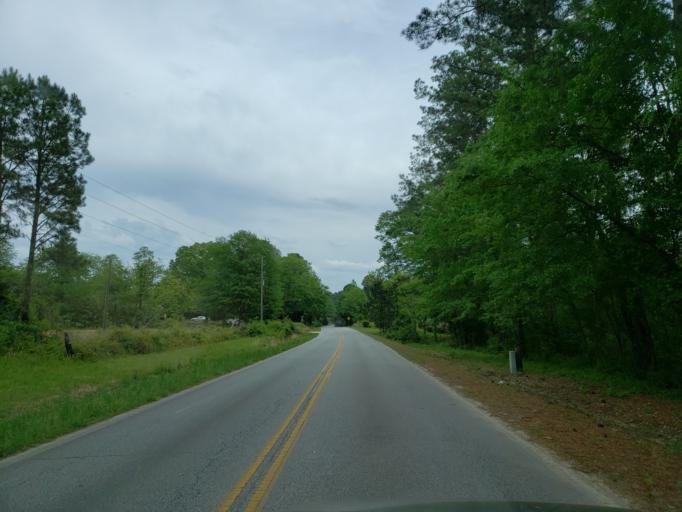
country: US
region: Georgia
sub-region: Bibb County
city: West Point
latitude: 32.8211
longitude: -83.8663
